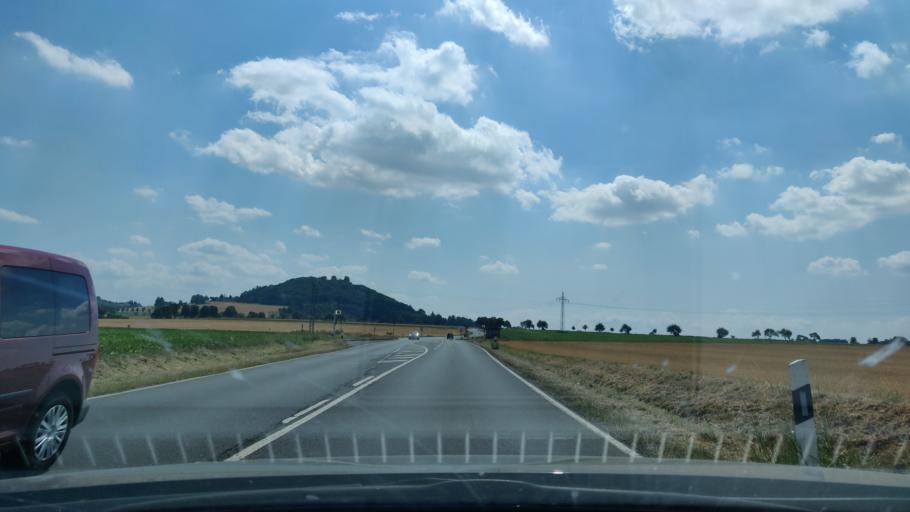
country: DE
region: Hesse
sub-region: Regierungsbezirk Kassel
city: Homberg
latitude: 51.0485
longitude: 9.3902
